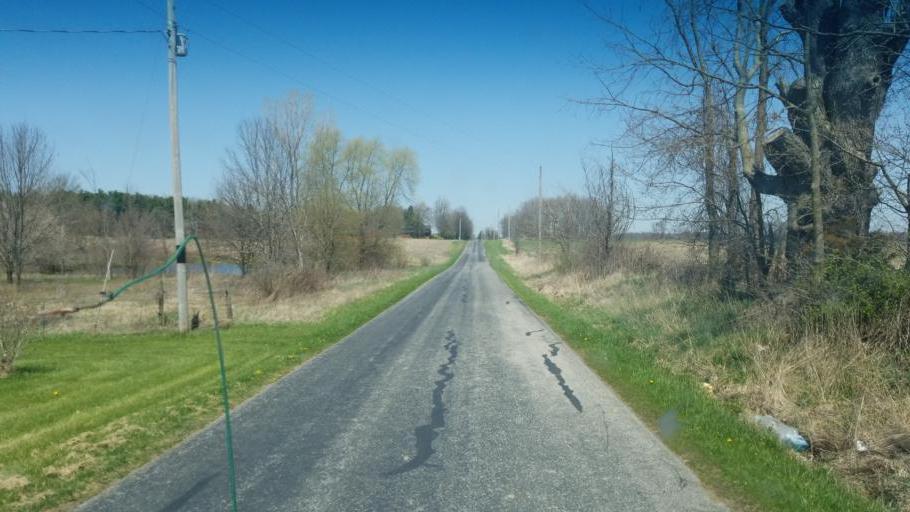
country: US
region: Ohio
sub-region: Huron County
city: New London
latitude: 41.0761
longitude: -82.4374
